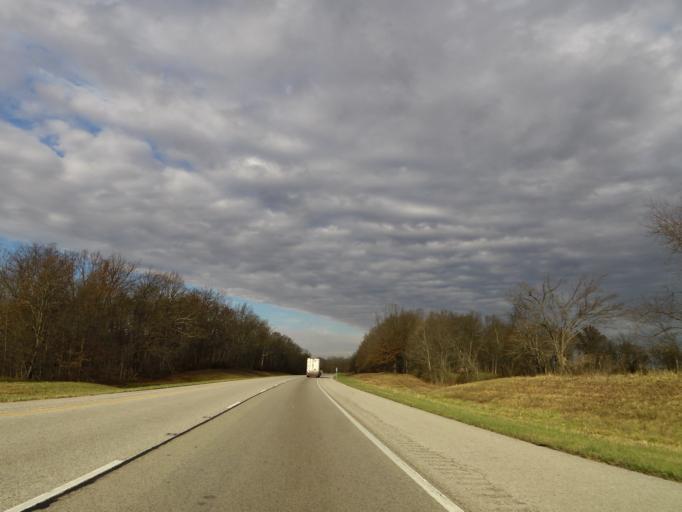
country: US
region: Illinois
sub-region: Washington County
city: Nashville
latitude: 38.4028
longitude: -89.4023
